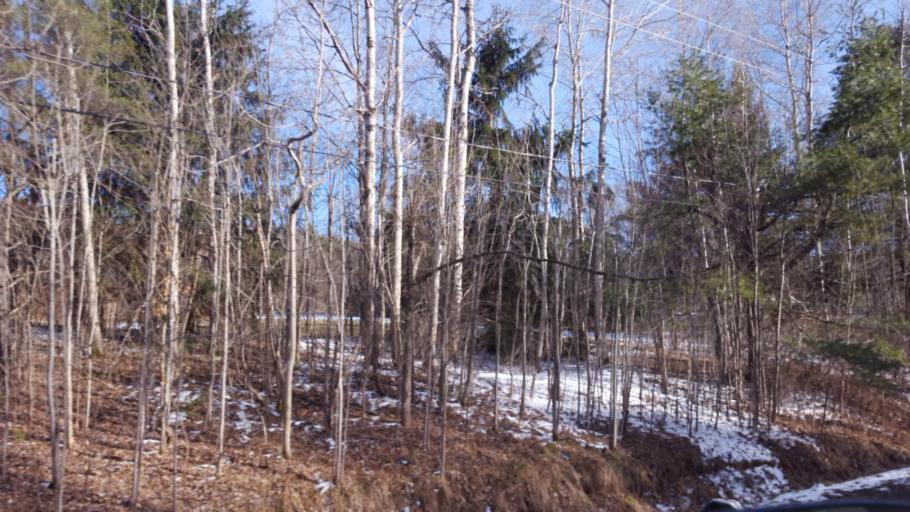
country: US
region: New York
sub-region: Allegany County
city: Wellsville
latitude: 42.0904
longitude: -77.9877
